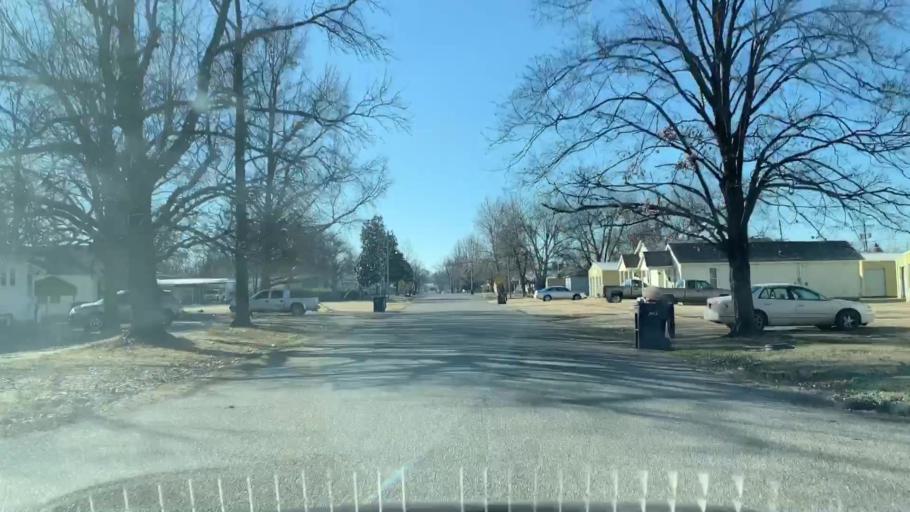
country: US
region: Kansas
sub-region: Cherokee County
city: Baxter Springs
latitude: 37.0173
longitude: -94.7346
